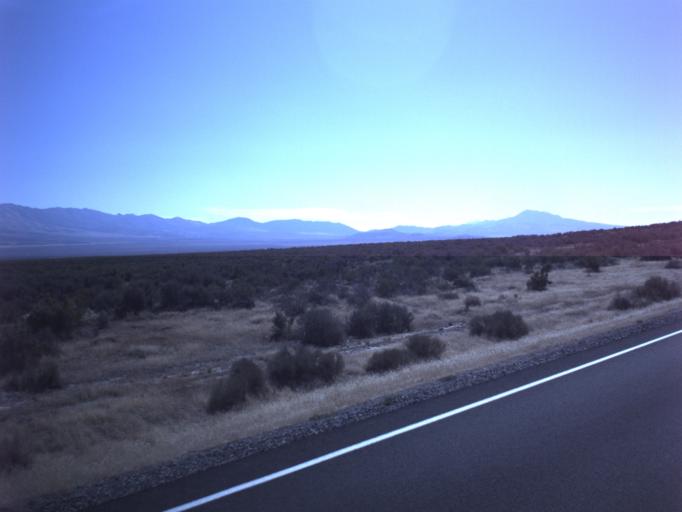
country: US
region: Utah
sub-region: Tooele County
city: Grantsville
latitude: 40.2930
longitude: -112.7424
